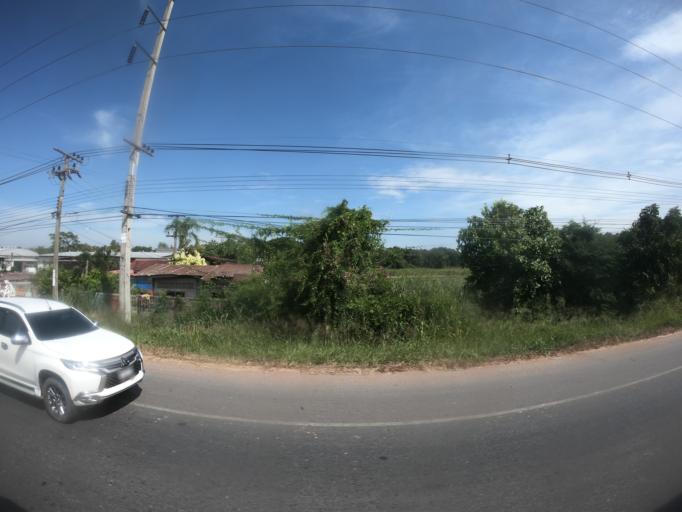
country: TH
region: Maha Sarakham
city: Chiang Yuen
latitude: 16.4429
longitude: 102.9692
